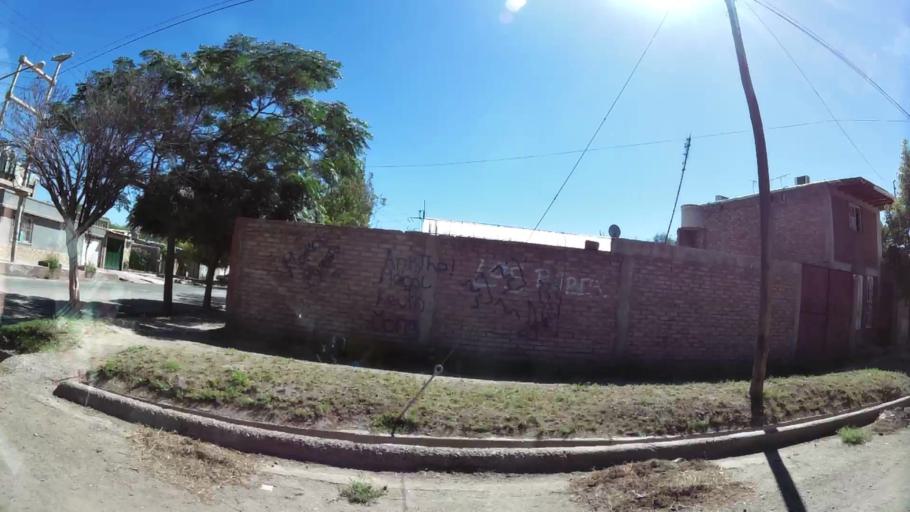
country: AR
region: Mendoza
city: Las Heras
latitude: -32.8284
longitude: -68.8224
